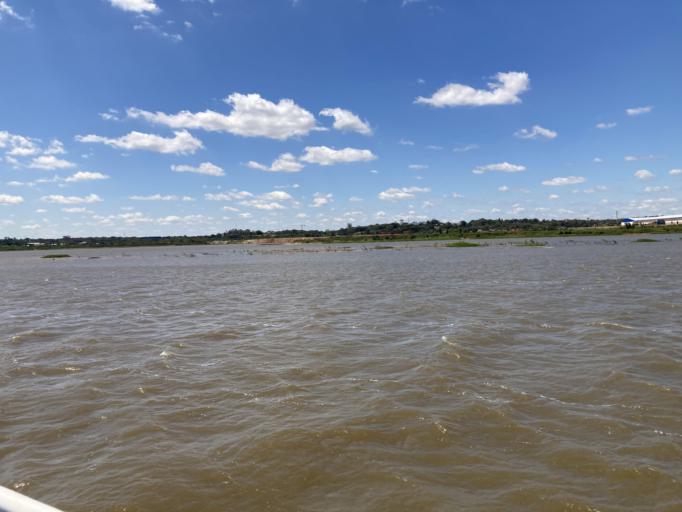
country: PY
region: Central
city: Colonia Mariano Roque Alonso
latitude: -25.2103
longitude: -57.5718
